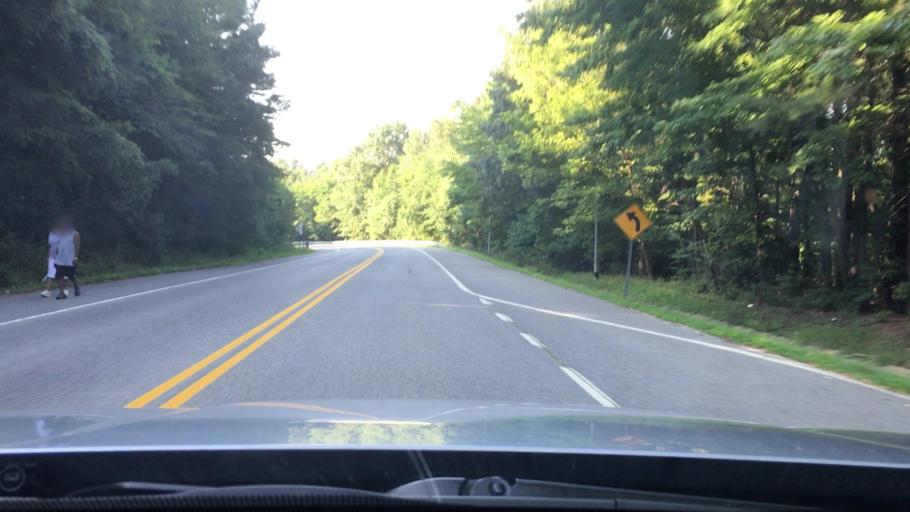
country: US
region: Maryland
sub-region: Prince George's County
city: Glenn Dale
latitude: 38.9927
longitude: -76.7904
